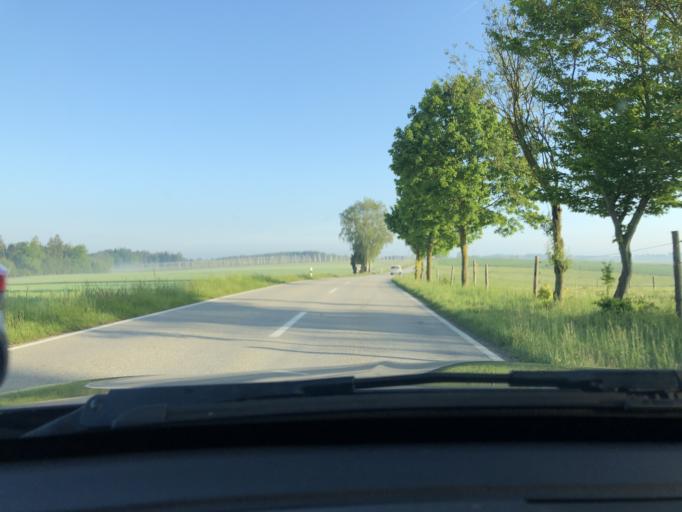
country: DE
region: Bavaria
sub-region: Upper Bavaria
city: Kirchdorf
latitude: 48.4773
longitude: 11.6340
